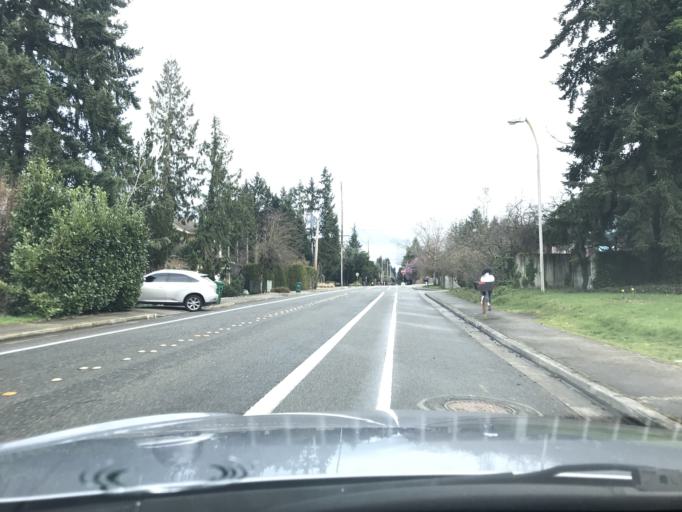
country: US
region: Washington
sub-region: King County
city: Redmond
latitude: 47.6471
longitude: -122.1110
